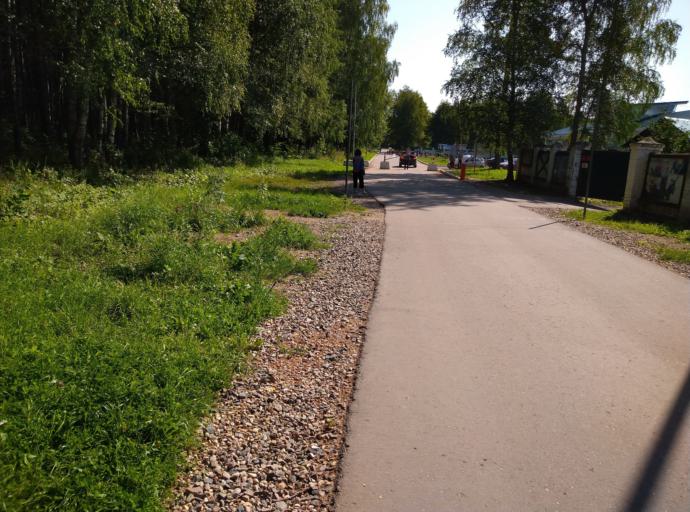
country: RU
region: Kostroma
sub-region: Kostromskoy Rayon
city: Kostroma
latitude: 57.7910
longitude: 40.9654
